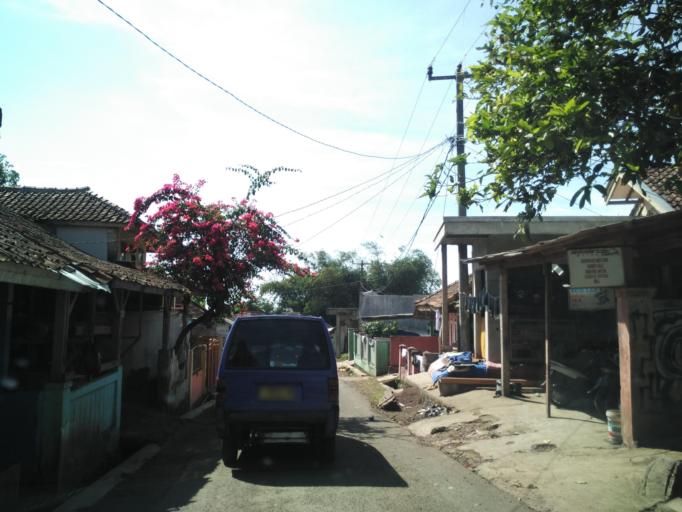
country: ID
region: West Java
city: Sukabumi
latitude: -6.8329
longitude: 107.0648
